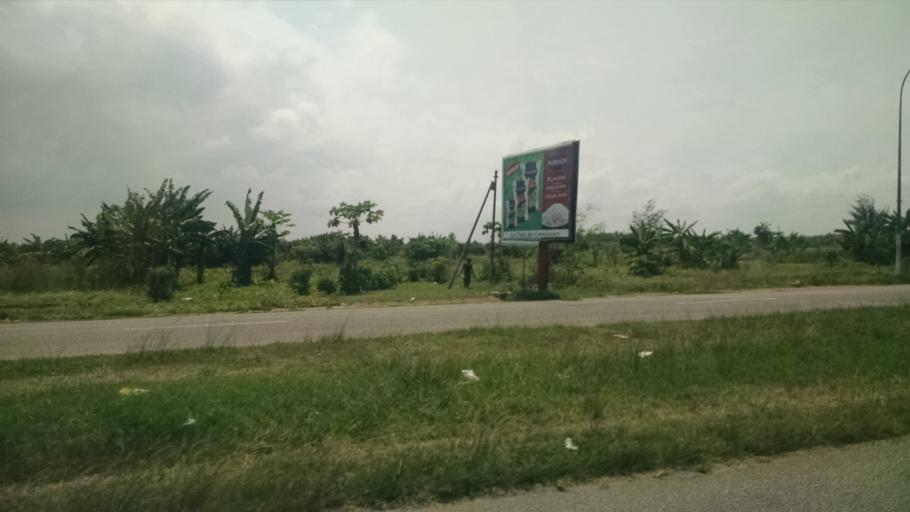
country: CI
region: Lagunes
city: Abidjan
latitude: 5.2638
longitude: -3.9512
